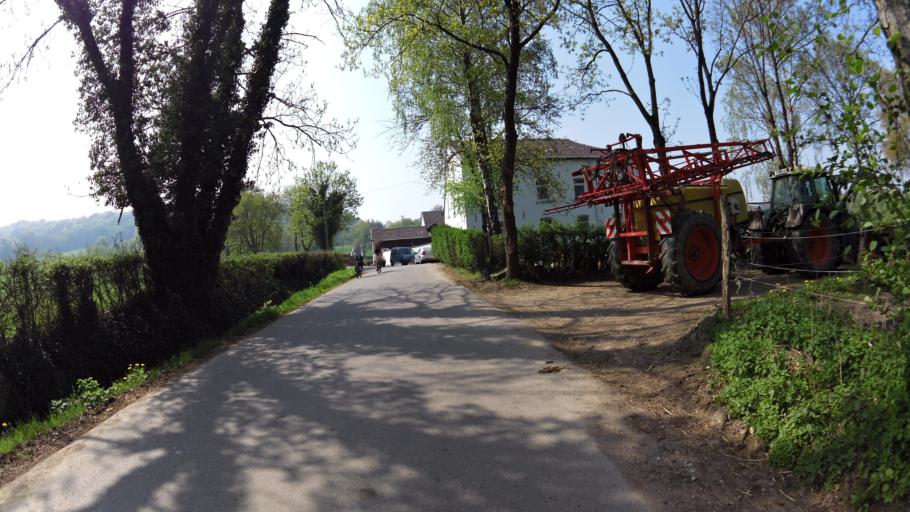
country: DE
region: North Rhine-Westphalia
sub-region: Regierungsbezirk Koln
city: Aachen
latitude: 50.7952
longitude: 6.0771
